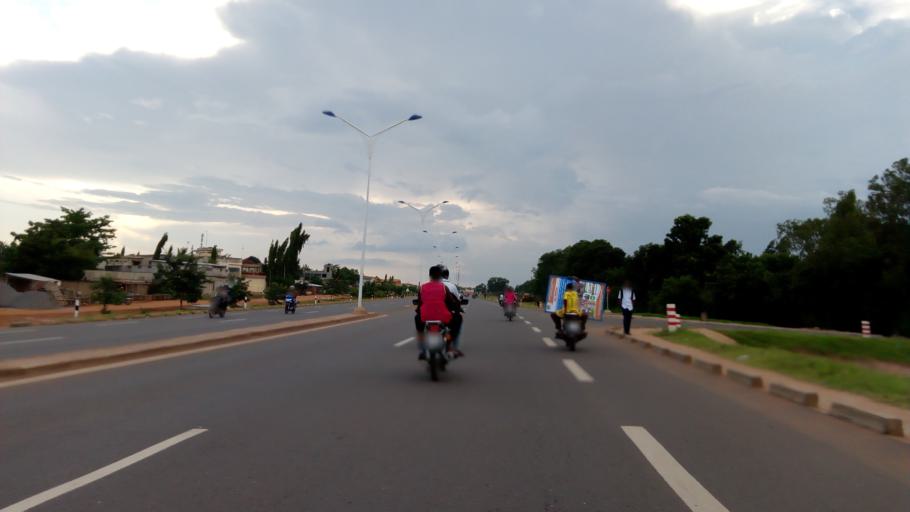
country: TG
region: Maritime
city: Lome
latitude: 6.2446
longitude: 1.1907
